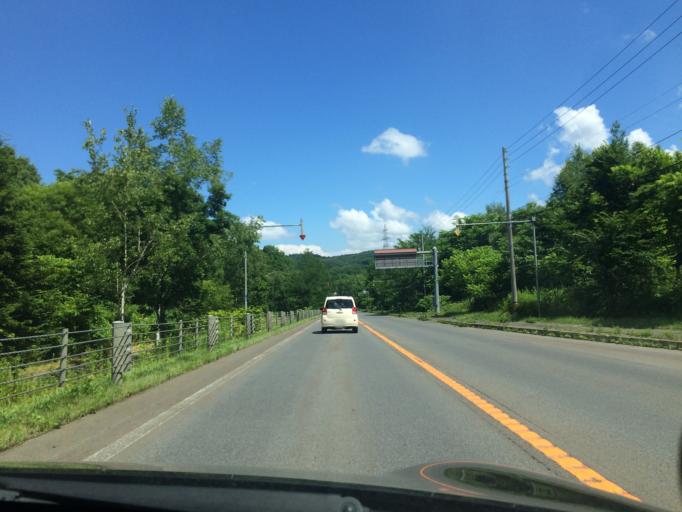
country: JP
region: Hokkaido
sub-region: Asahikawa-shi
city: Asahikawa
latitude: 43.7530
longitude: 142.2629
